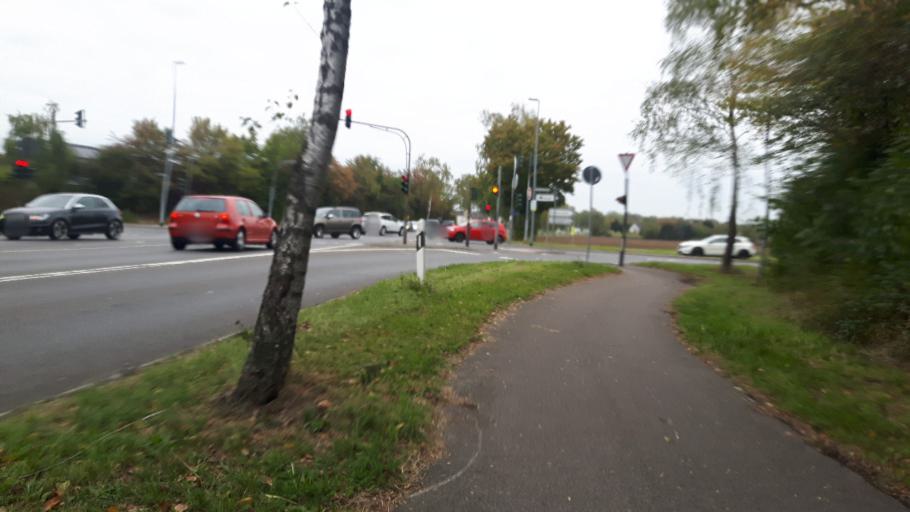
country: DE
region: North Rhine-Westphalia
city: Sankt Augustin
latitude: 50.7618
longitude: 7.1747
